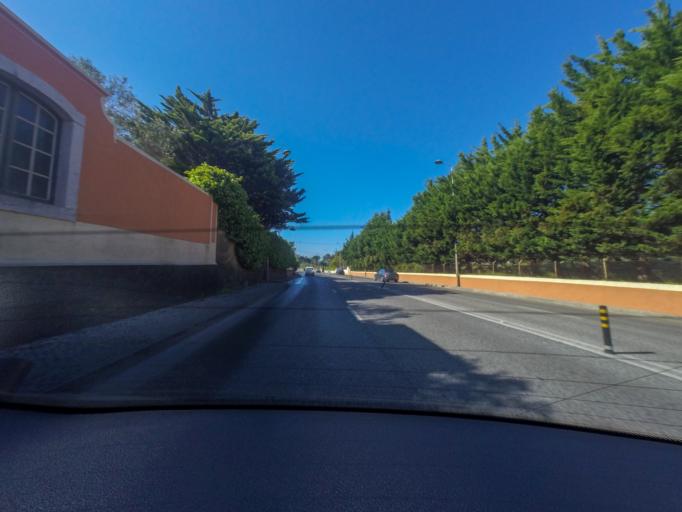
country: PT
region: Lisbon
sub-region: Sintra
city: Sintra
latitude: 38.7672
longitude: -9.3852
